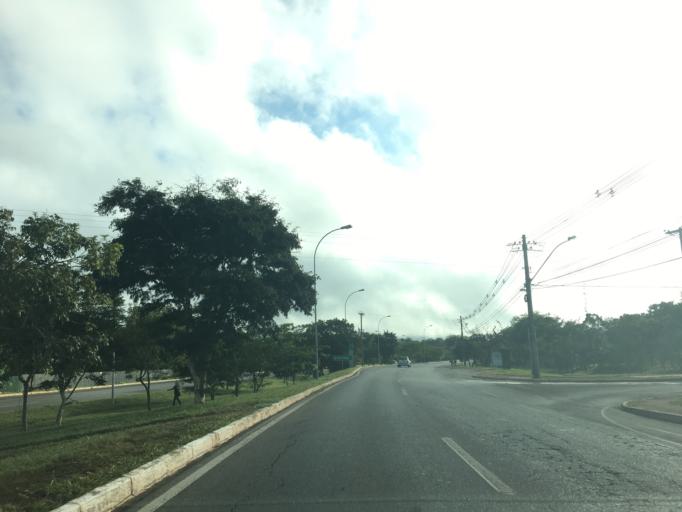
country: BR
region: Federal District
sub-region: Brasilia
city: Brasilia
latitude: -15.8134
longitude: -47.8053
